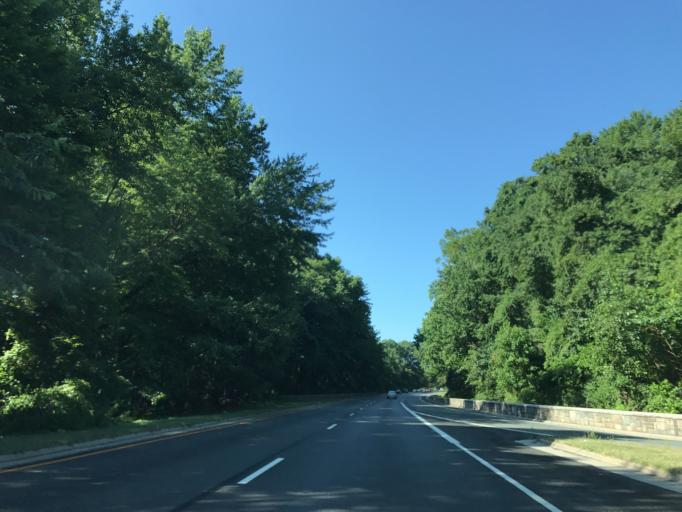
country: US
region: Maryland
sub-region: Prince George's County
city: Greenbelt
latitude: 39.0051
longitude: -76.8640
